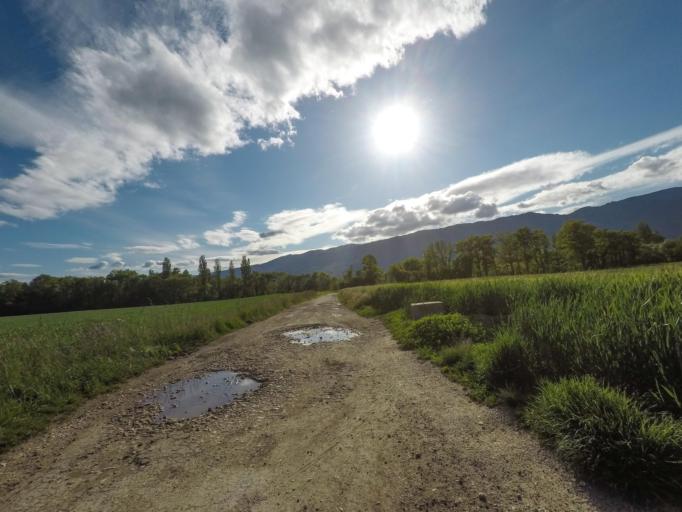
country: FR
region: Rhone-Alpes
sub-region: Departement de l'Ain
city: Chevry
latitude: 46.2621
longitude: 6.0551
